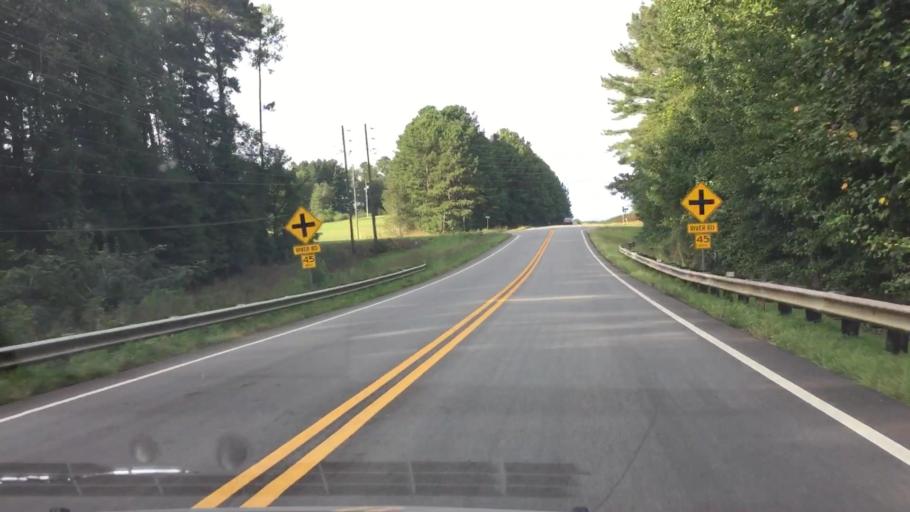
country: US
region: Georgia
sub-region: Newton County
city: Oakwood
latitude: 33.4746
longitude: -83.9632
